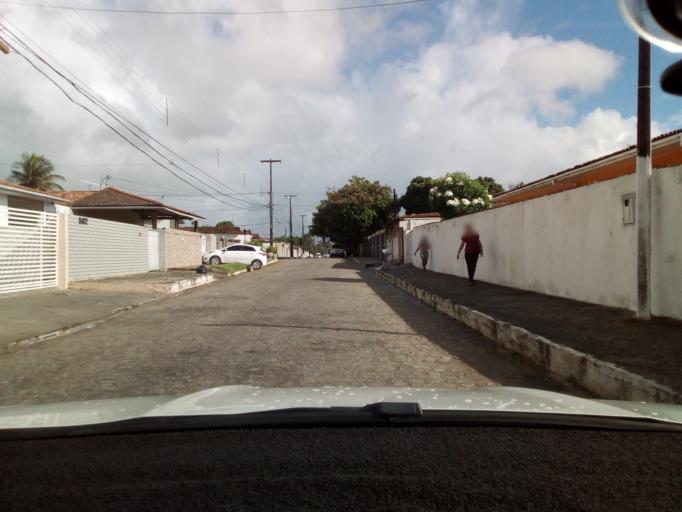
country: BR
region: Paraiba
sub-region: Joao Pessoa
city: Joao Pessoa
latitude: -7.1646
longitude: -34.8716
